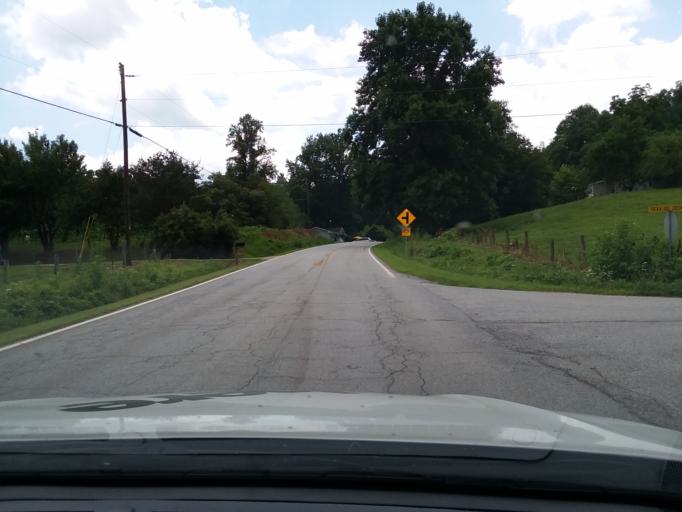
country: US
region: Georgia
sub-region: Rabun County
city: Mountain City
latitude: 34.8934
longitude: -83.2926
